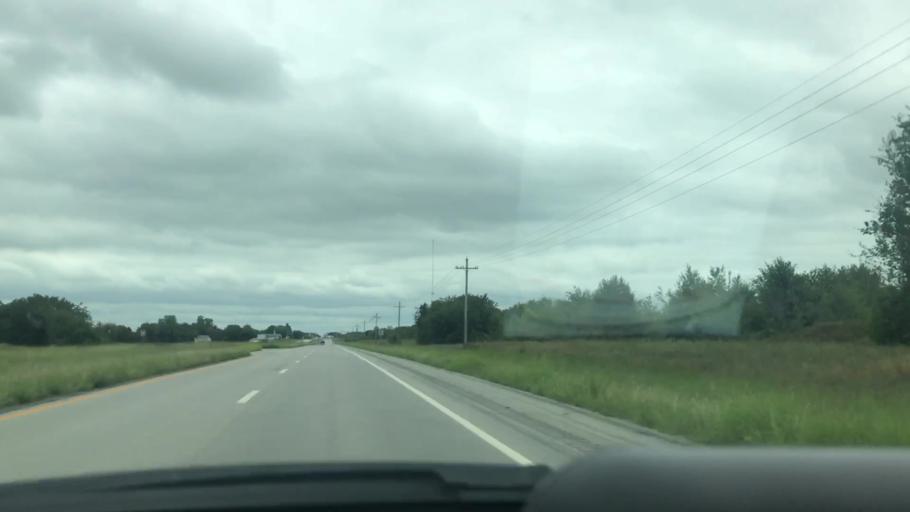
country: US
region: Oklahoma
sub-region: Mayes County
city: Pryor
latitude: 36.4150
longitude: -95.2797
